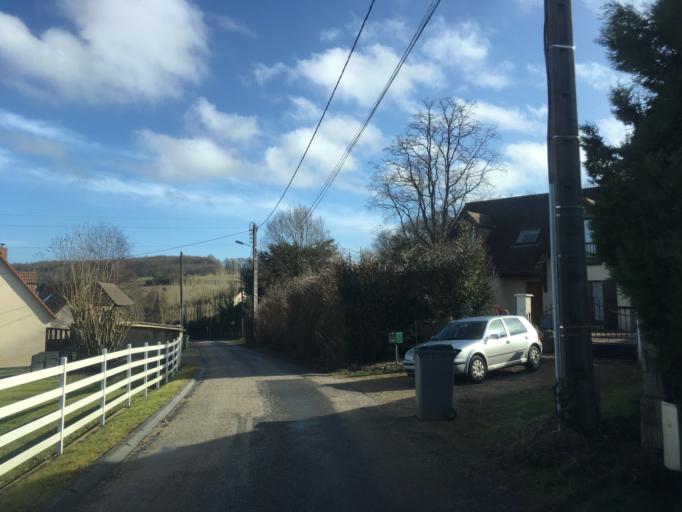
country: FR
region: Haute-Normandie
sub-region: Departement de l'Eure
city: La Chapelle-Reanville
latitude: 49.1215
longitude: 1.4017
